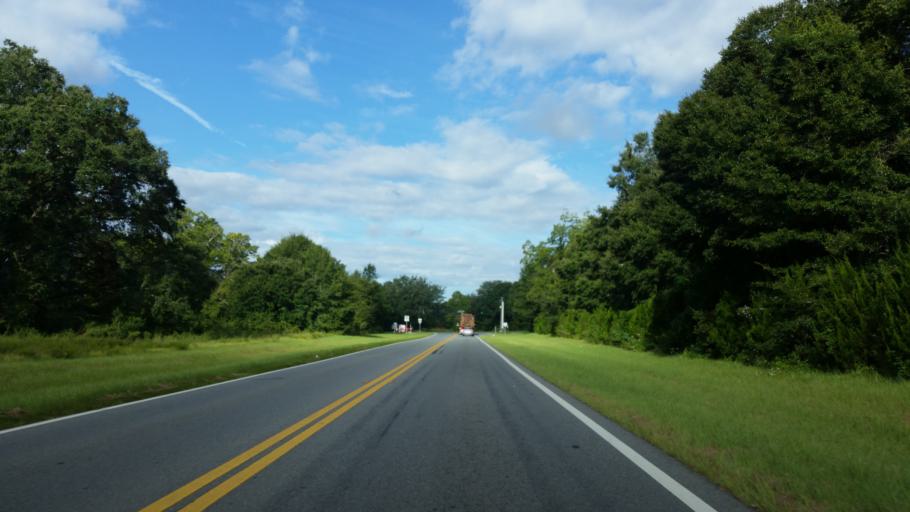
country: US
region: Florida
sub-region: Santa Rosa County
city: Wallace
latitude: 30.6448
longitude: -87.1781
